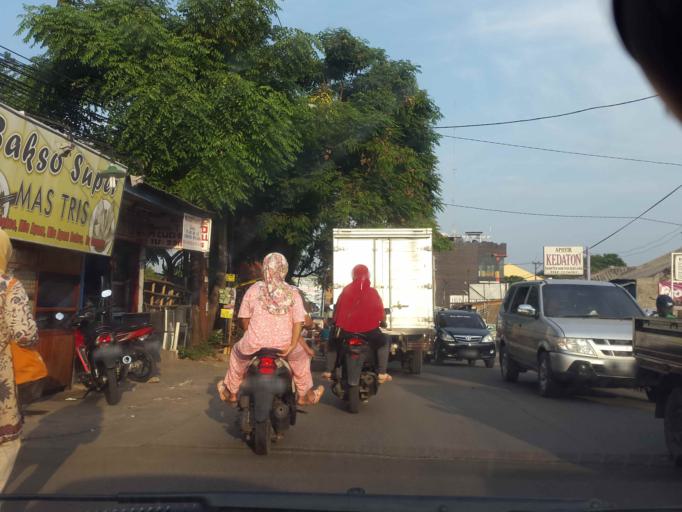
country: ID
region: Banten
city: South Tangerang
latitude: -6.2624
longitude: 106.7224
